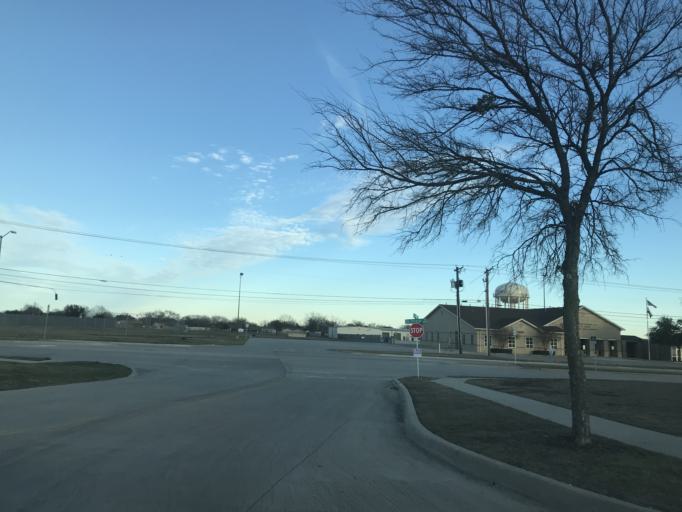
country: US
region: Texas
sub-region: Tarrant County
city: Saginaw
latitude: 32.8779
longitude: -97.3914
